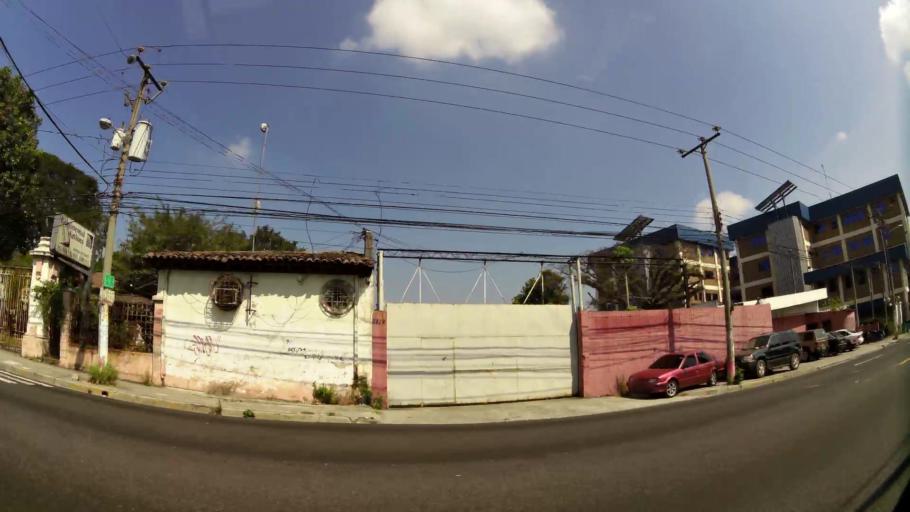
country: SV
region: San Salvador
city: San Salvador
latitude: 13.6968
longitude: -89.2202
